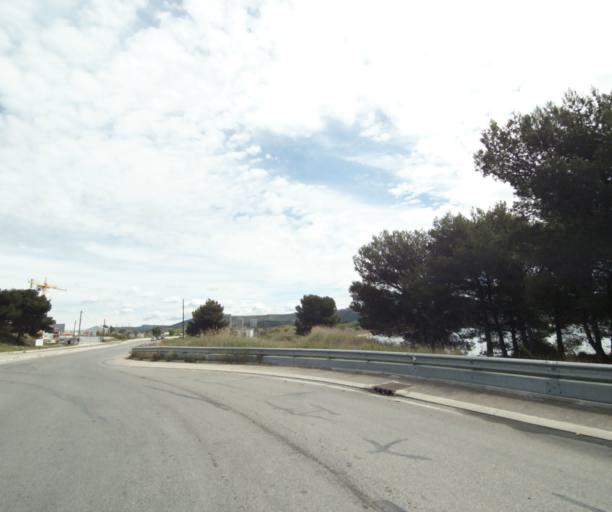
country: FR
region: Provence-Alpes-Cote d'Azur
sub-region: Departement des Bouches-du-Rhone
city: Rognac
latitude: 43.4922
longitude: 5.2049
